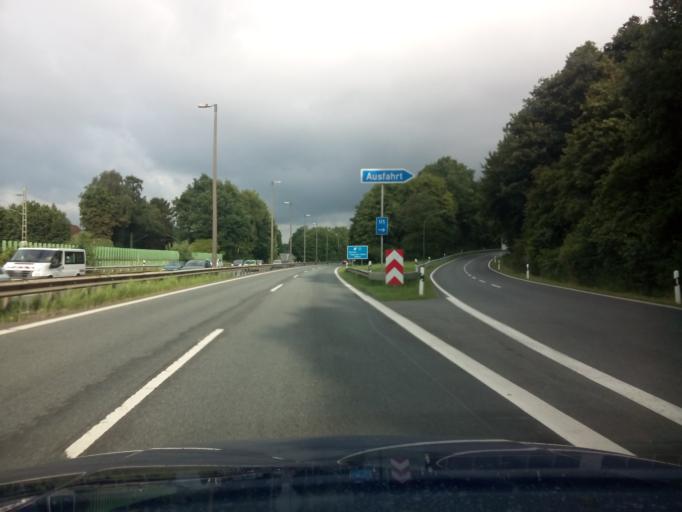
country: DE
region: Lower Saxony
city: Lemwerder
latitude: 53.1728
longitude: 8.6574
